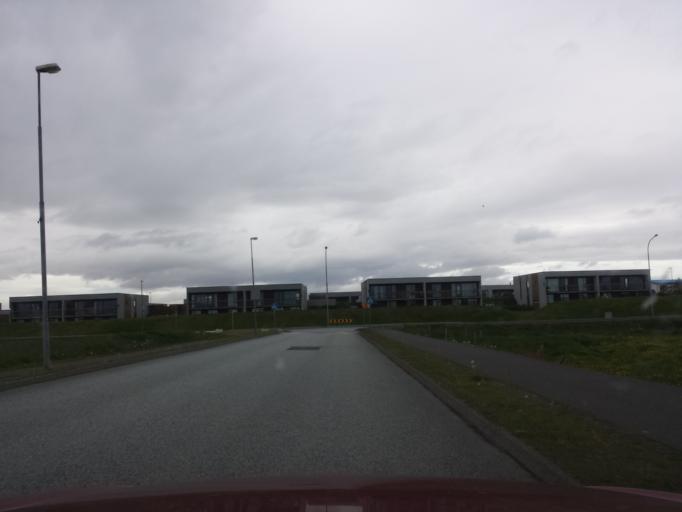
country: IS
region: Capital Region
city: Alftanes
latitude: 64.1015
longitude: -22.0174
